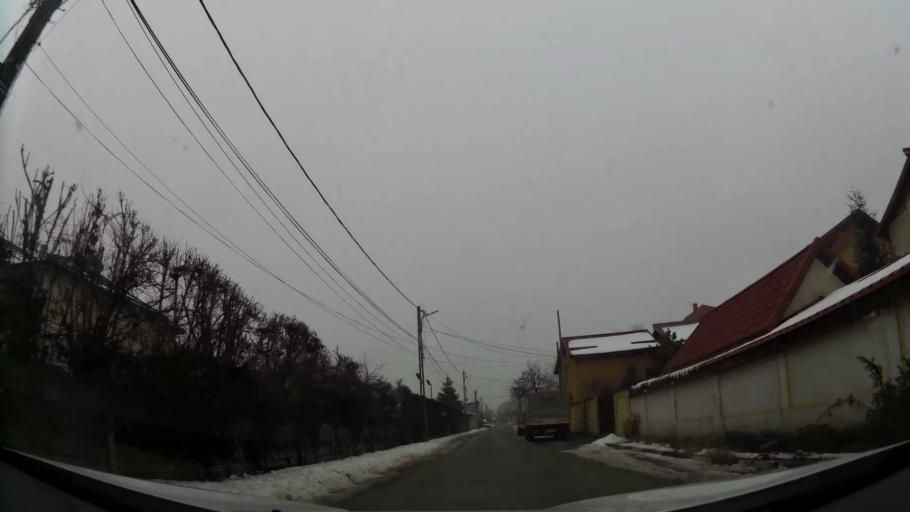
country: RO
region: Ilfov
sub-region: Comuna Chiajna
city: Rosu
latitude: 44.4534
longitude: 26.0042
